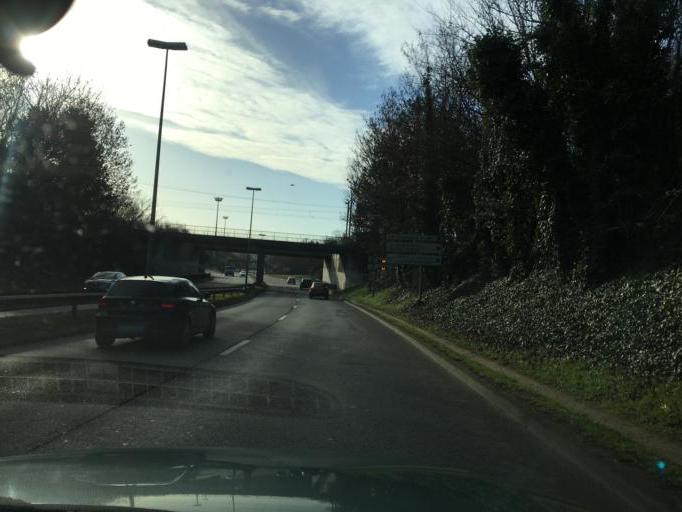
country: FR
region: Centre
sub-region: Departement du Loiret
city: Saint-Jean-de-la-Ruelle
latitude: 47.9087
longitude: 1.8679
